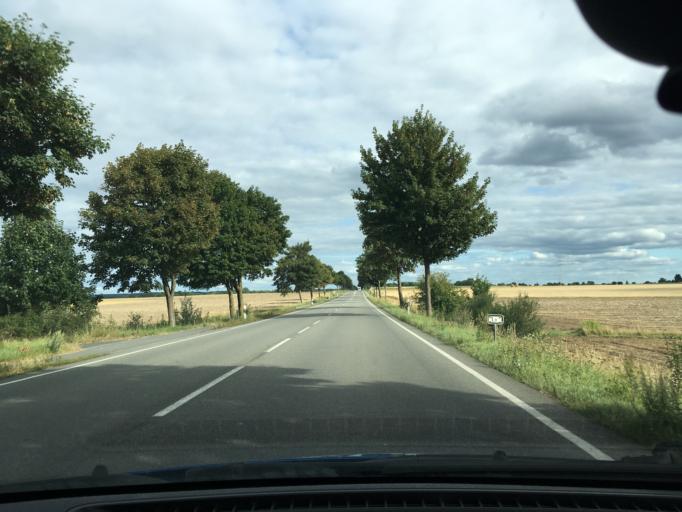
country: DE
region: Lower Saxony
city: Neu Wulmstorf
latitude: 53.4381
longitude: 9.7680
